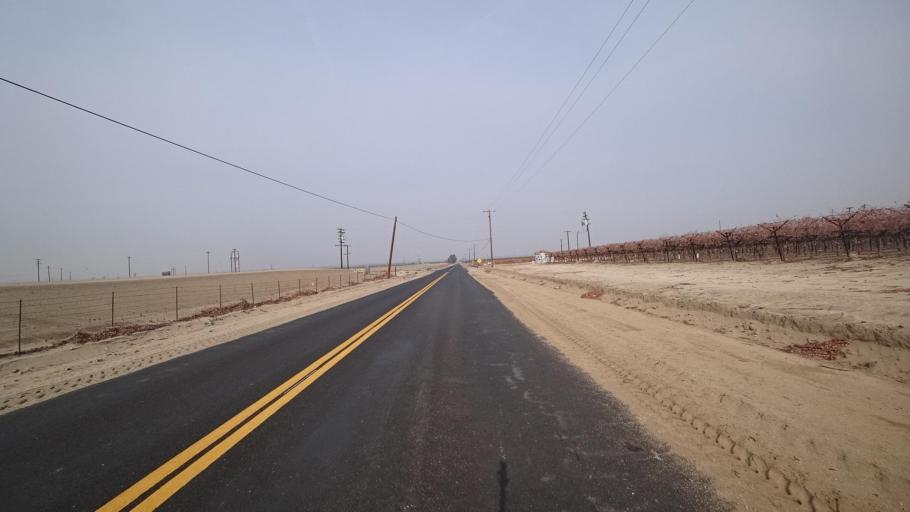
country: US
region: California
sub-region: Kern County
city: Arvin
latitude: 35.1356
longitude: -118.8507
